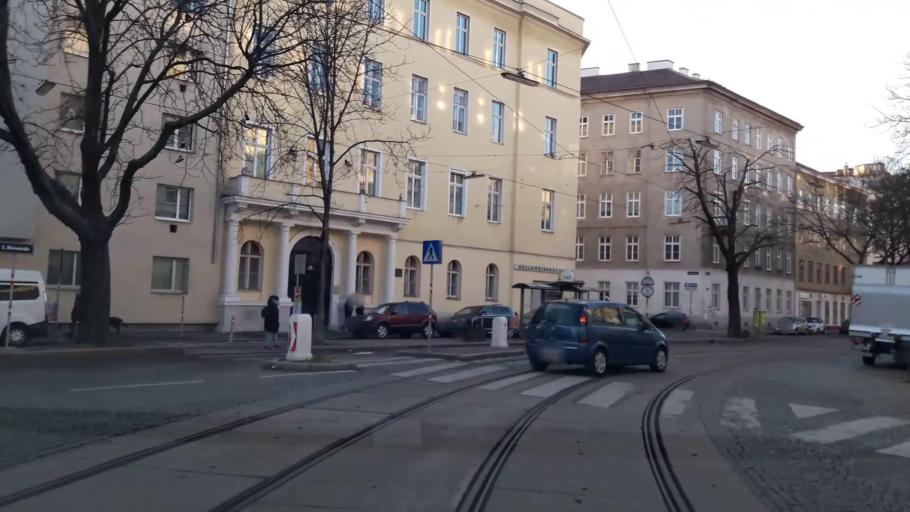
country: AT
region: Vienna
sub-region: Wien Stadt
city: Vienna
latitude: 48.2205
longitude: 16.3862
